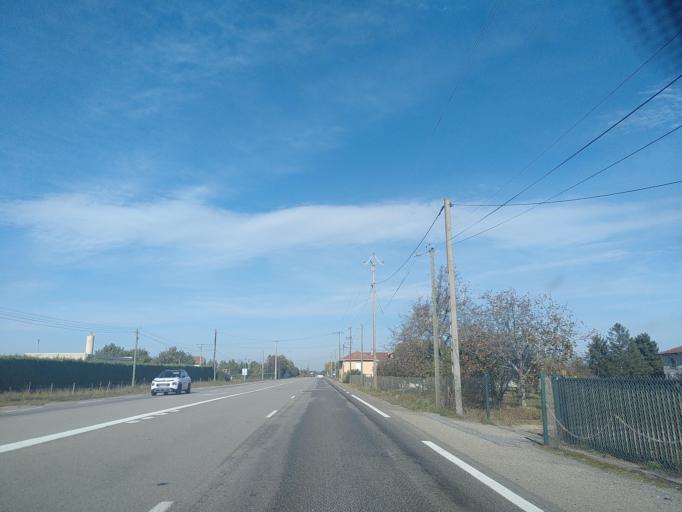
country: FR
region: Rhone-Alpes
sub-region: Departement de la Drome
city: Andancette
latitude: 45.2451
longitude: 4.8208
